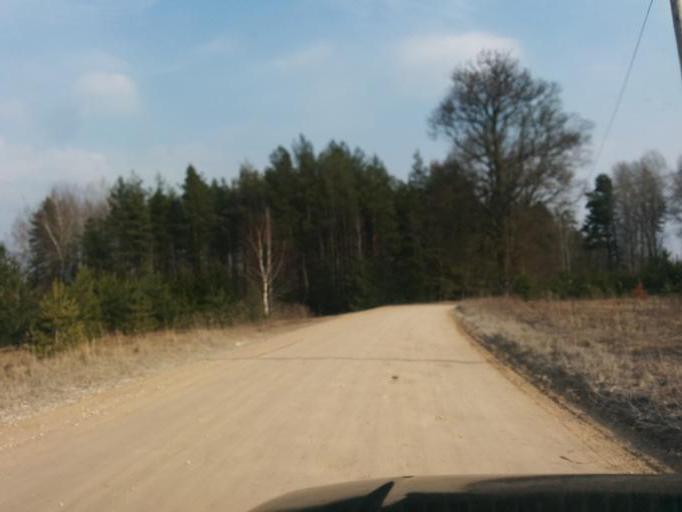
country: LV
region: Olaine
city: Olaine
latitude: 56.7910
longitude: 24.0021
